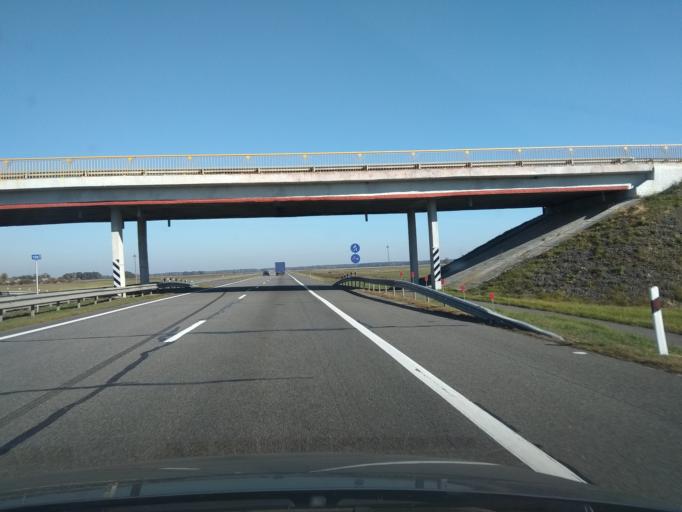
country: BY
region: Brest
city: Ivatsevichy
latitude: 52.7242
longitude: 25.4368
